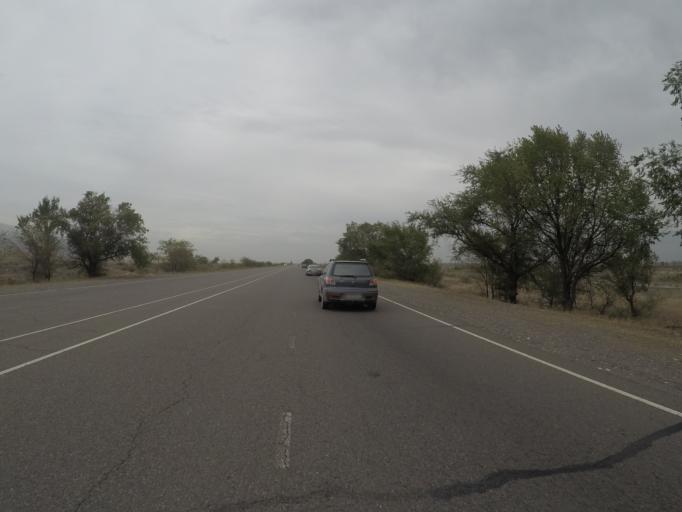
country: KG
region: Chuy
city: Tokmok
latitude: 42.8329
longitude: 75.4441
